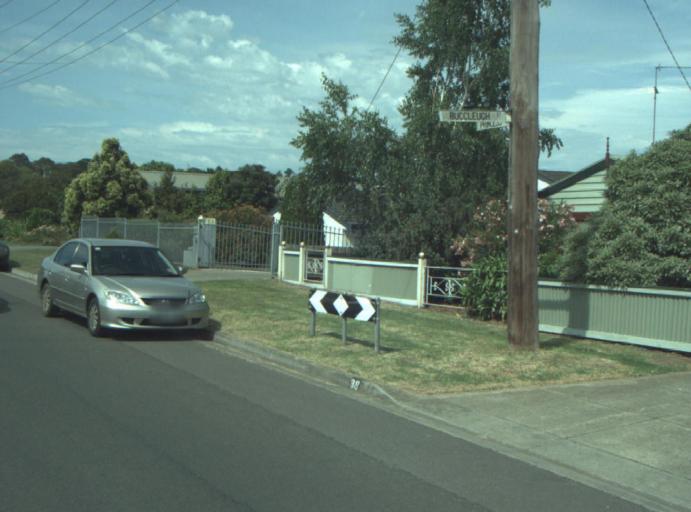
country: AU
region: Victoria
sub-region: Greater Geelong
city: Clifton Springs
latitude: -38.1807
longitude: 144.5693
